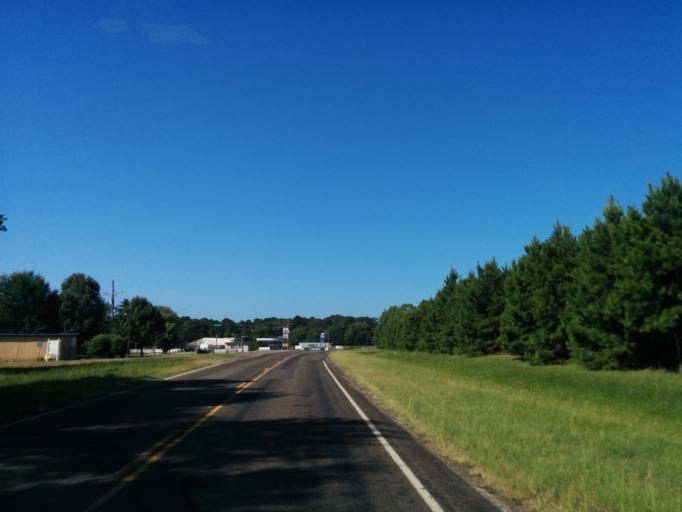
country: US
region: Texas
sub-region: Sabine County
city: Milam
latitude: 31.4516
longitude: -93.7639
